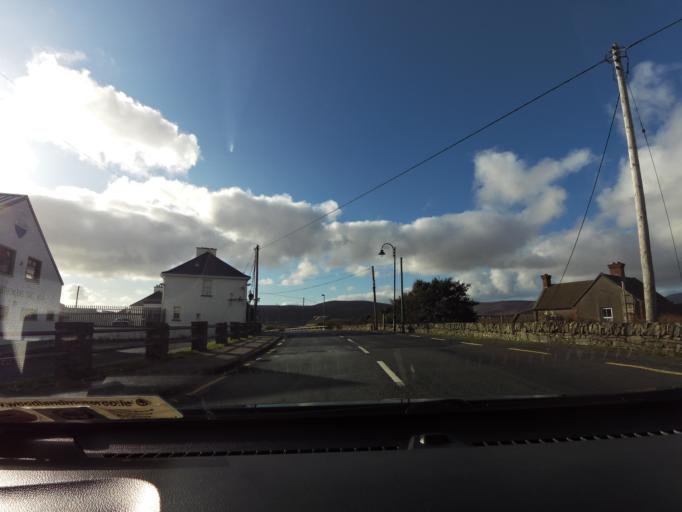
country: IE
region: Connaught
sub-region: Maigh Eo
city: Belmullet
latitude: 53.9339
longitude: -9.9179
